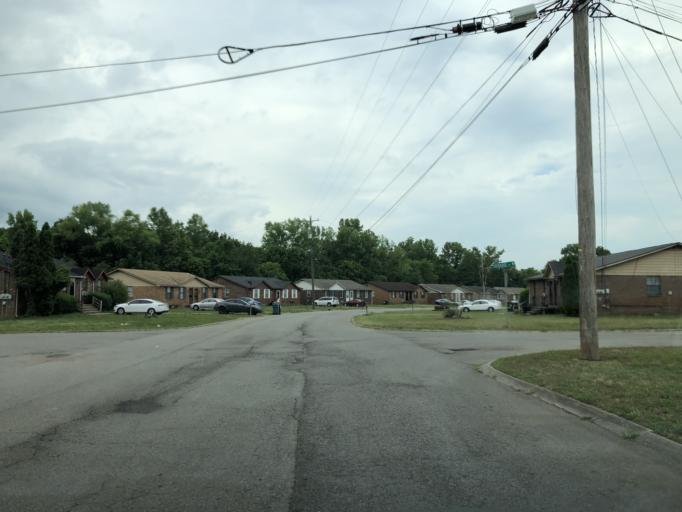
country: US
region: Tennessee
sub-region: Davidson County
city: Goodlettsville
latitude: 36.2599
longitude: -86.7659
